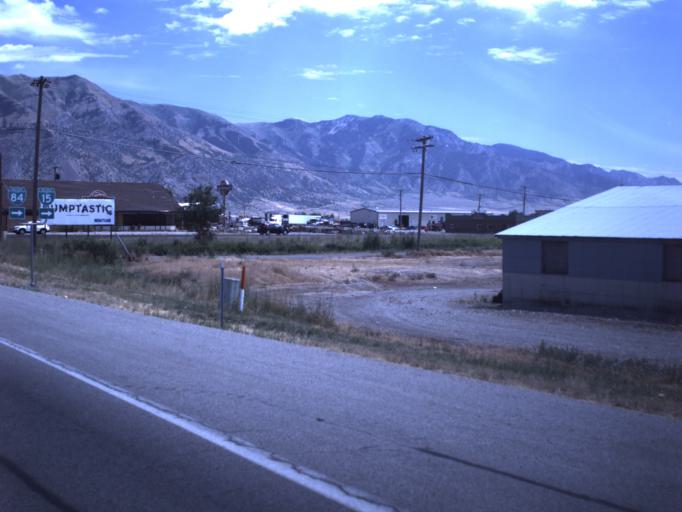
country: US
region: Utah
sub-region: Box Elder County
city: Tremonton
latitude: 41.7123
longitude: -112.1436
